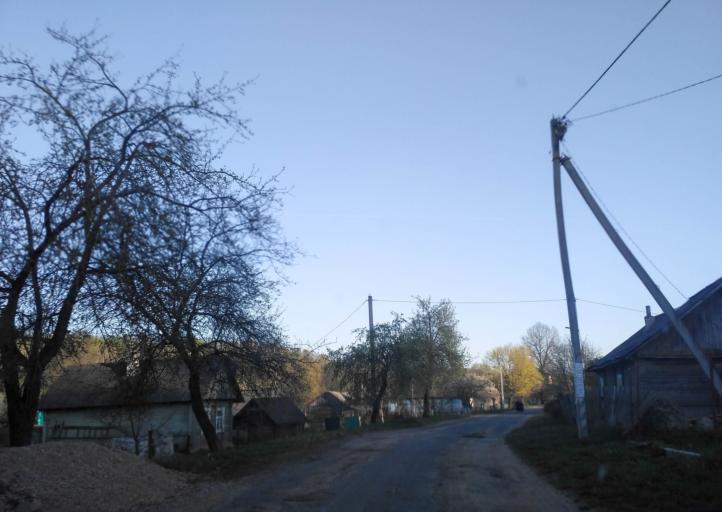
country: BY
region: Minsk
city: Pyatryshki
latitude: 54.0991
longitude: 27.1954
